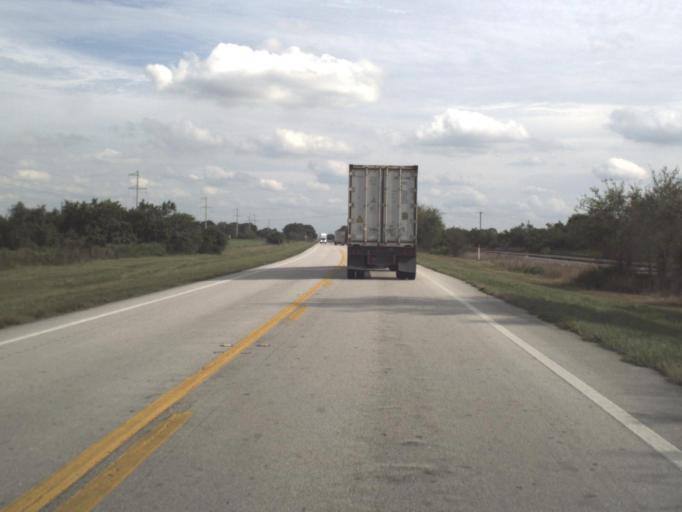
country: US
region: Florida
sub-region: Okeechobee County
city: Taylor Creek
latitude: 27.2104
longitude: -80.7550
